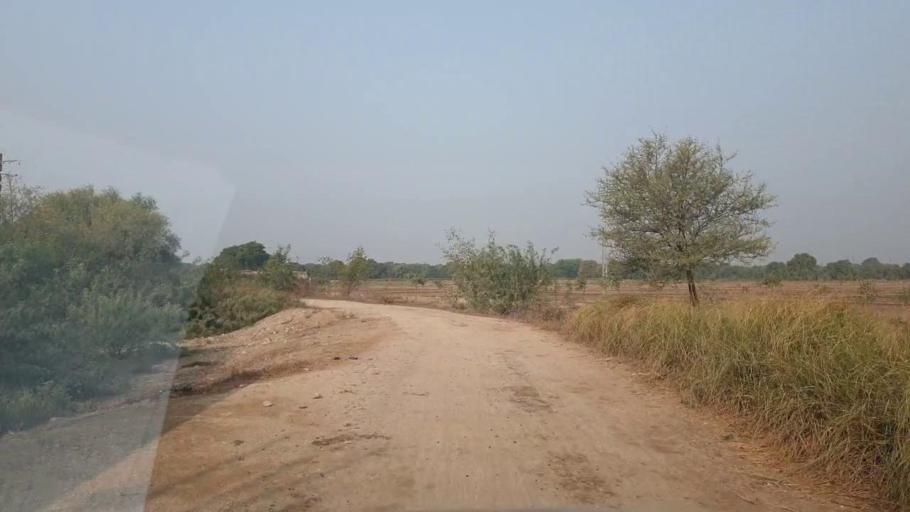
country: PK
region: Sindh
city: Tando Jam
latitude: 25.3305
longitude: 68.5223
